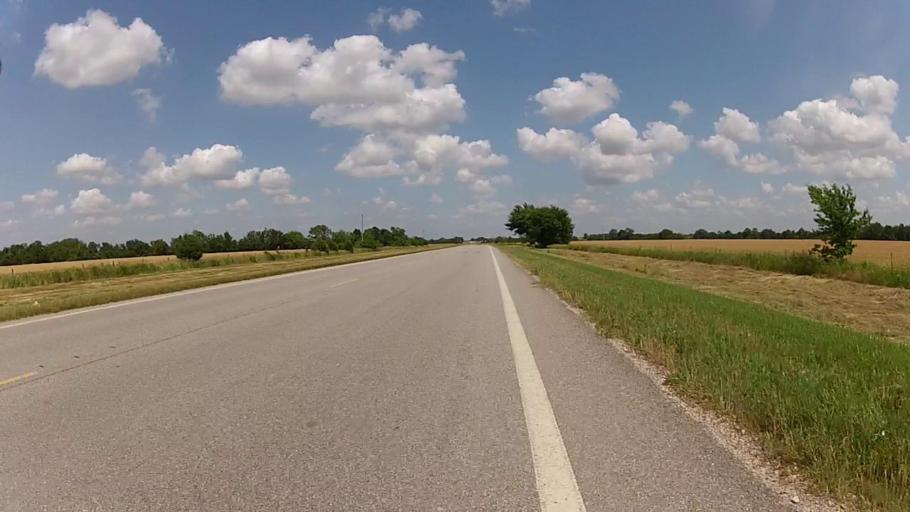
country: US
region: Kansas
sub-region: Labette County
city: Altamont
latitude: 37.1931
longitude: -95.2337
